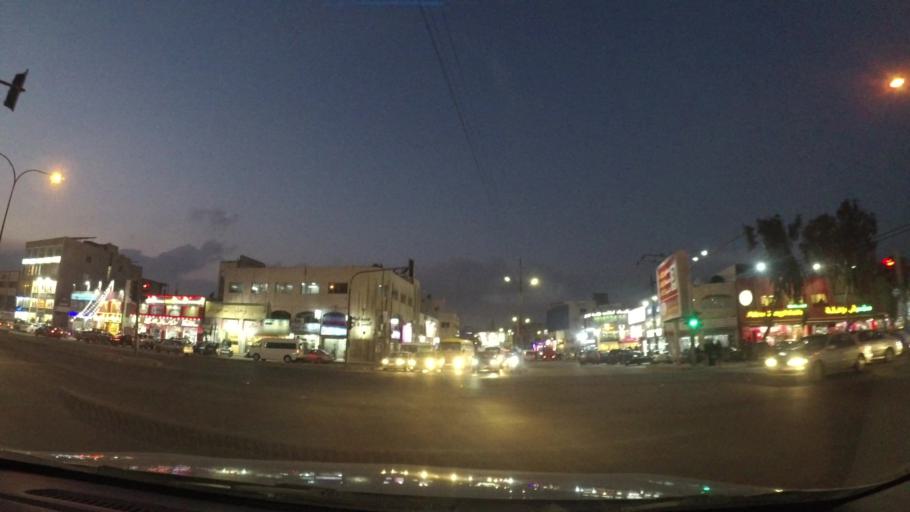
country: JO
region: Amman
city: Al Bunayyat ash Shamaliyah
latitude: 31.8957
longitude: 35.9142
